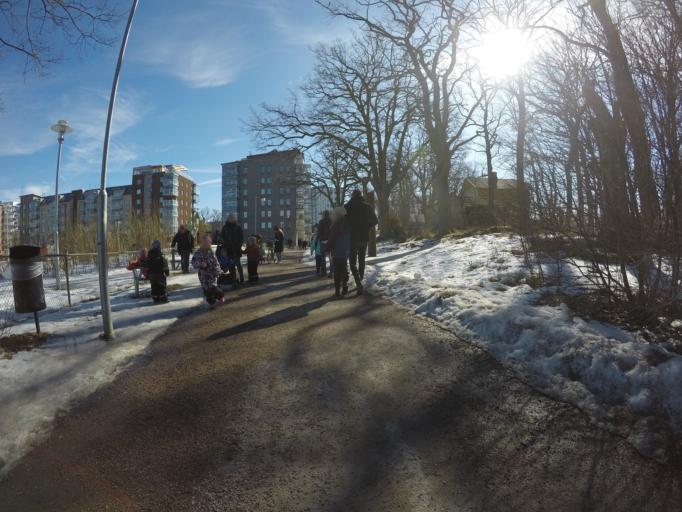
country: SE
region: Vaestmanland
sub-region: Vasteras
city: Vasteras
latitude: 59.6034
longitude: 16.5734
